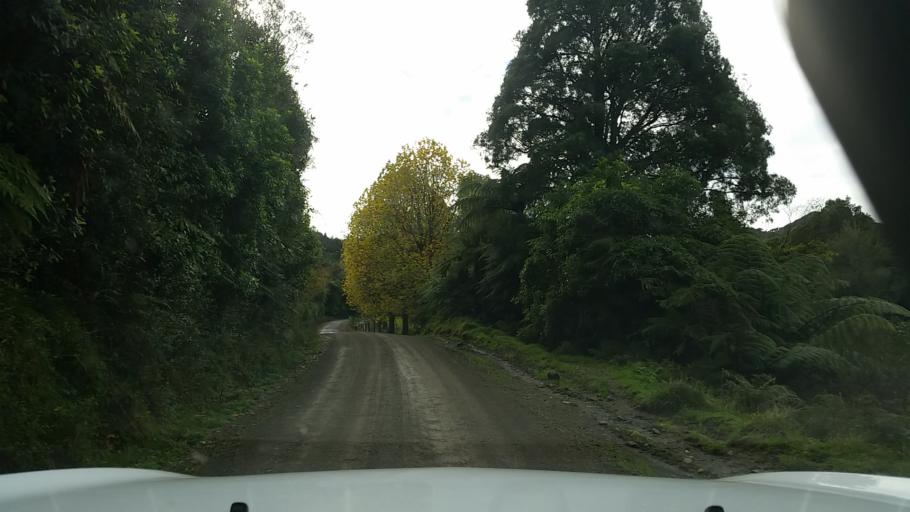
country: NZ
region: Taranaki
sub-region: New Plymouth District
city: Waitara
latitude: -38.8155
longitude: 174.6157
